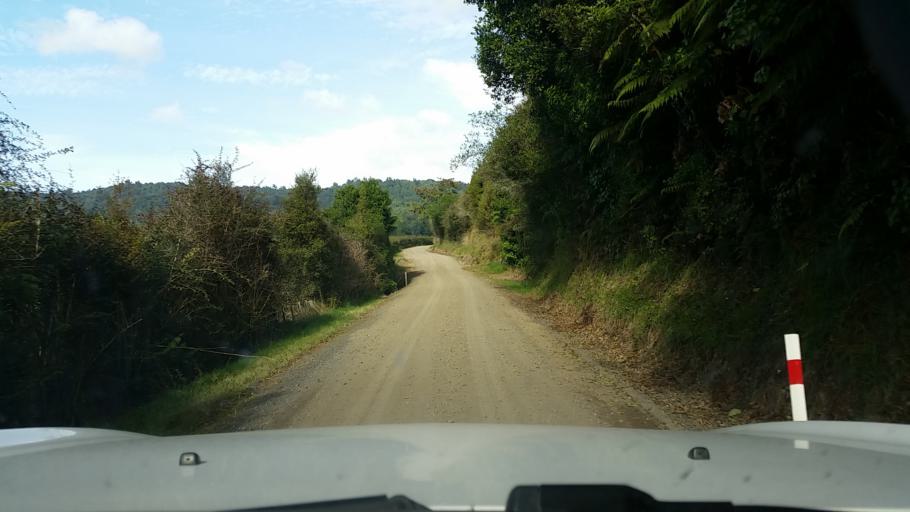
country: NZ
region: Waikato
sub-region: Matamata-Piako District
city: Matamata
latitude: -37.8170
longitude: 175.6317
